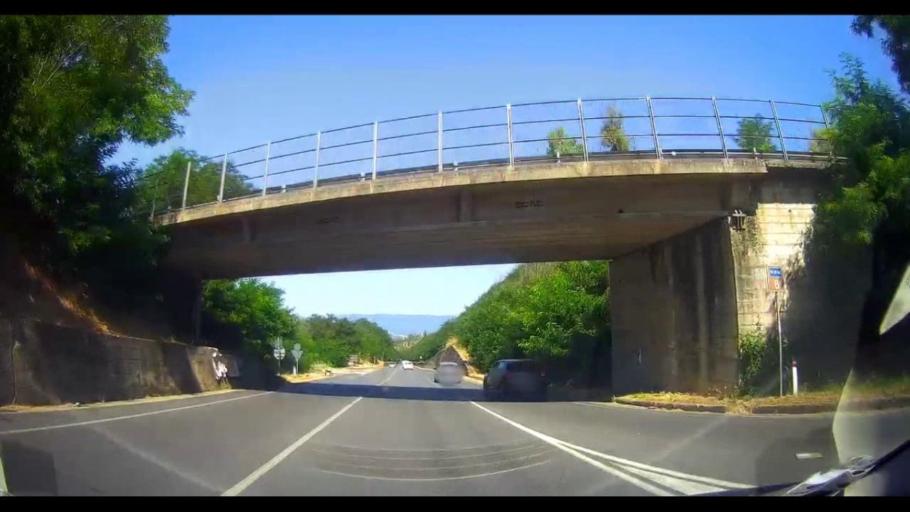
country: IT
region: Calabria
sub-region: Provincia di Cosenza
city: Rovito
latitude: 39.2966
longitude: 16.3043
